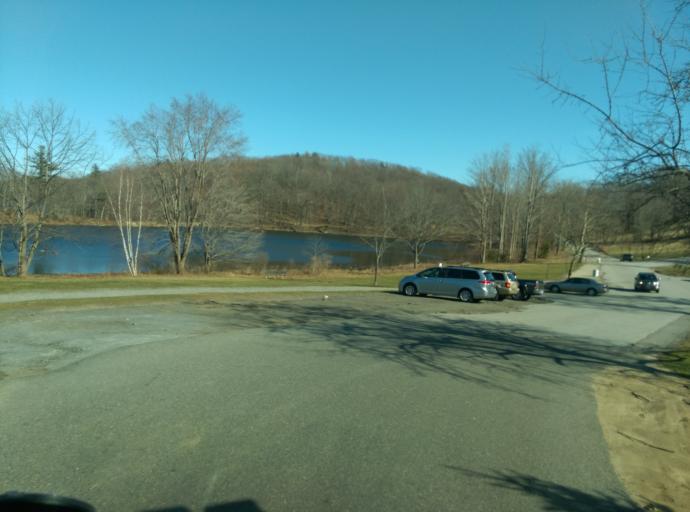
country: US
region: Massachusetts
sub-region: Essex County
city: Haverhill
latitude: 42.7911
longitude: -71.0691
